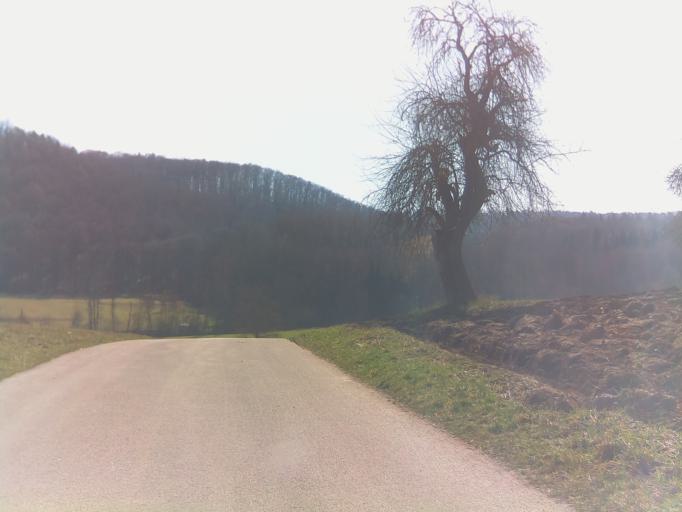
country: DE
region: Baden-Wuerttemberg
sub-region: Regierungsbezirk Stuttgart
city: Gartringen
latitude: 48.6215
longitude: 8.9152
